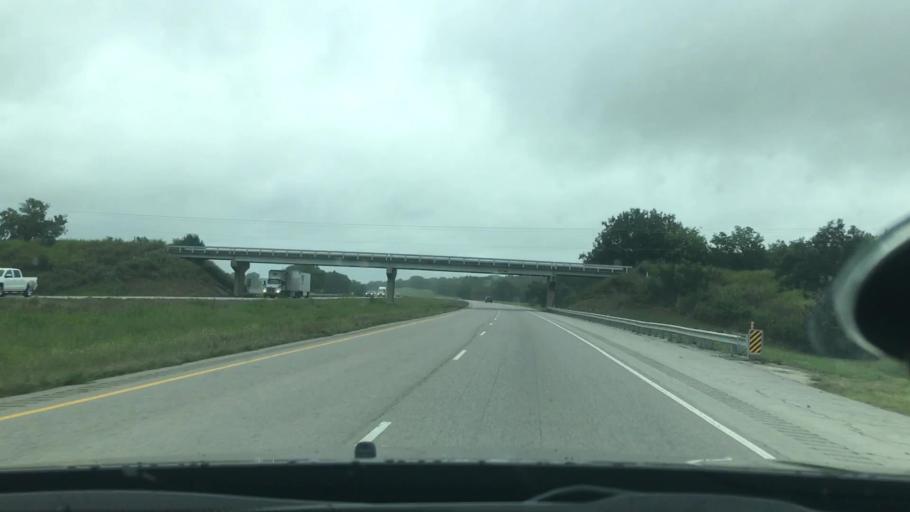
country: US
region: Oklahoma
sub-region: Okfuskee County
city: Boley
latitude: 35.3859
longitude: -96.4250
